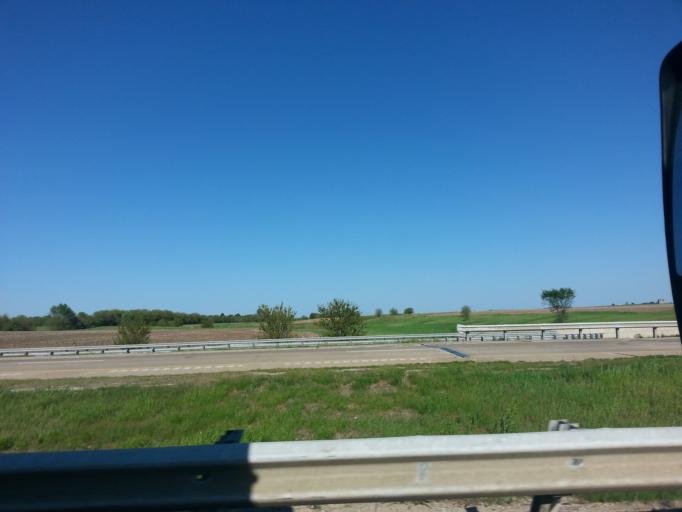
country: US
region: Illinois
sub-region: Marshall County
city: Wenona
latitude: 41.0923
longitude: -89.0674
